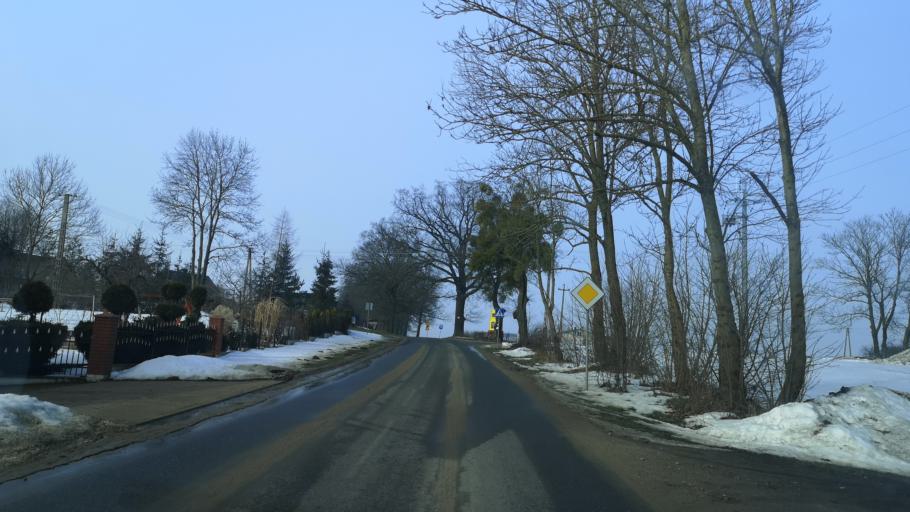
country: PL
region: Warmian-Masurian Voivodeship
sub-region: Powiat nowomiejski
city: Biskupiec
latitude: 53.5252
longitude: 19.3437
